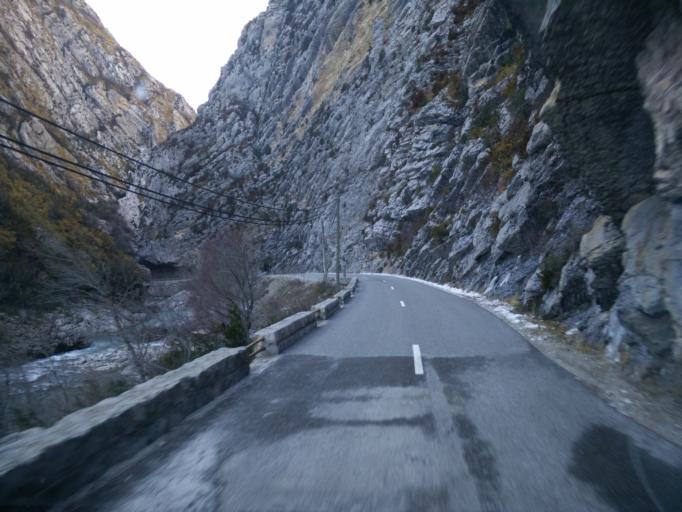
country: FR
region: Provence-Alpes-Cote d'Azur
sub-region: Departement des Alpes-de-Haute-Provence
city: Castellane
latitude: 43.8320
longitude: 6.4473
